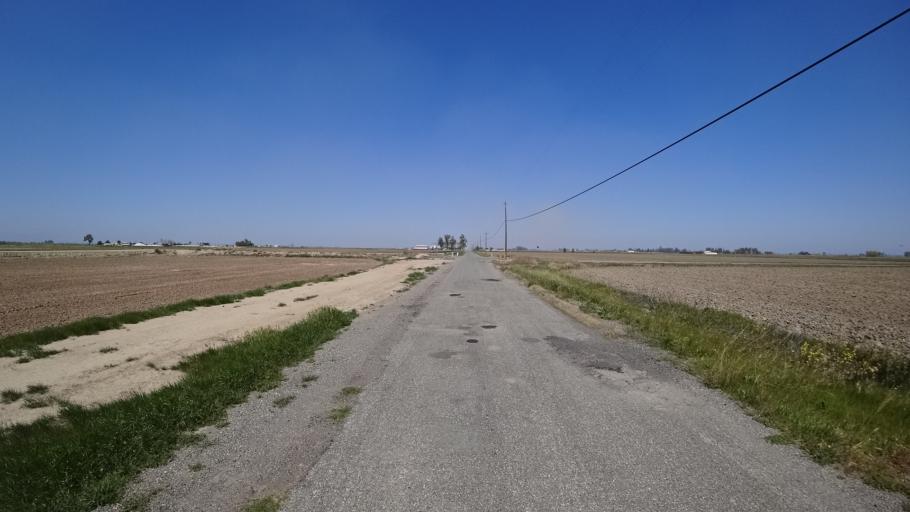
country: US
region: California
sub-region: Glenn County
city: Willows
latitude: 39.5304
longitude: -122.1124
